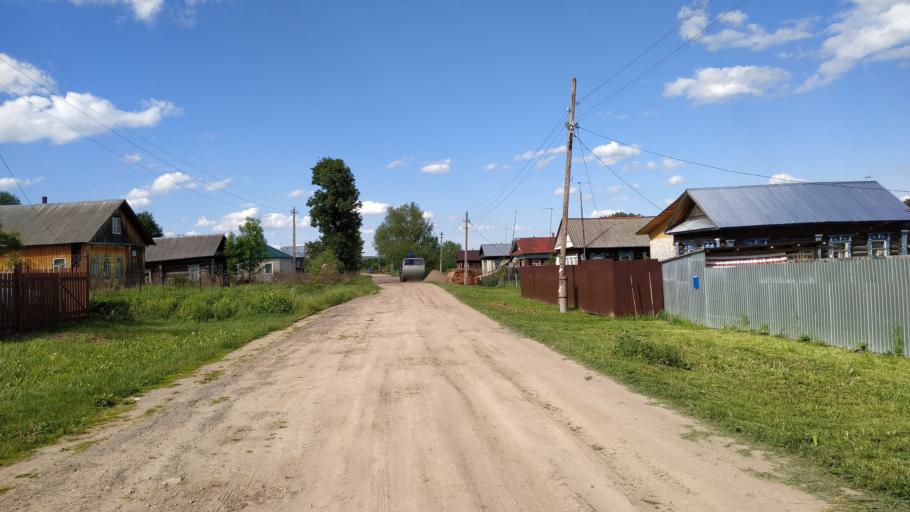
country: RU
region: Nizjnij Novgorod
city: Bogorodsk
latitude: 55.8856
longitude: 43.5575
